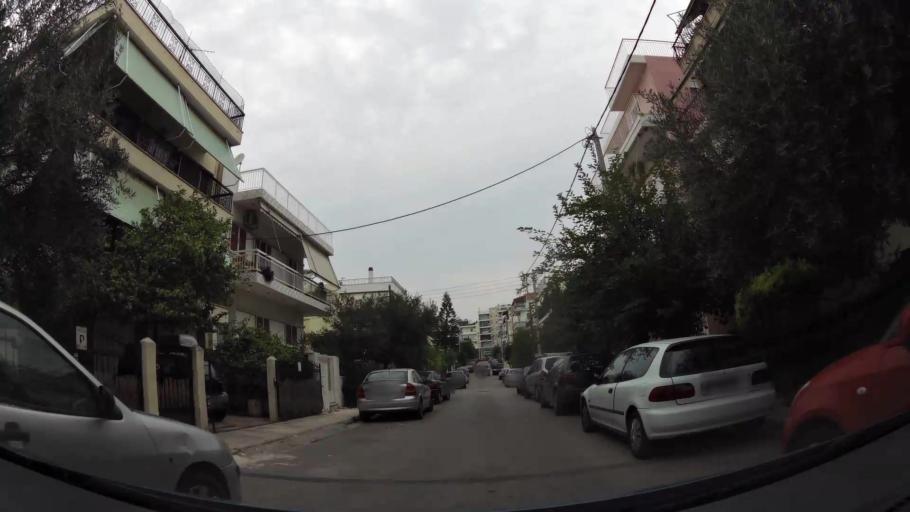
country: GR
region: Attica
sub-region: Nomarchia Athinas
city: Alimos
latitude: 37.9168
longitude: 23.7286
